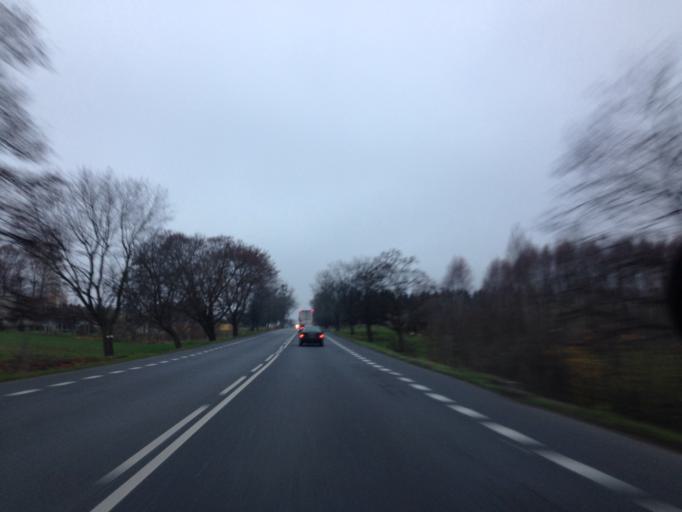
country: PL
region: Lodz Voivodeship
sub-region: Powiat zgierski
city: Strykow
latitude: 51.8400
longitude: 19.5540
